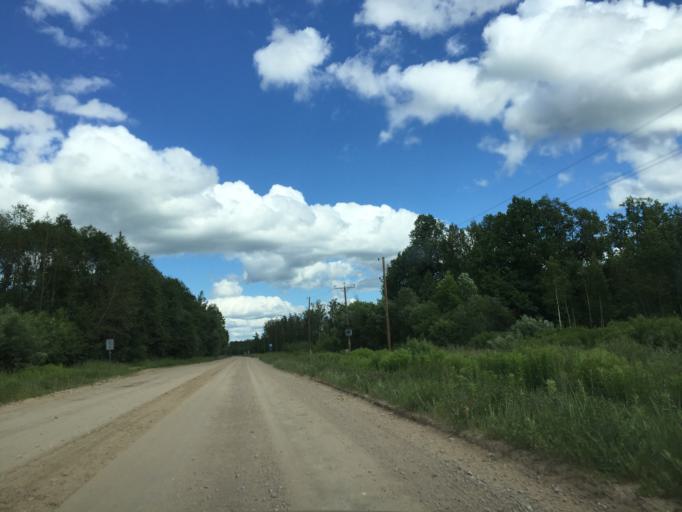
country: LV
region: Vecumnieki
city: Vecumnieki
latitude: 56.5030
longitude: 24.3801
